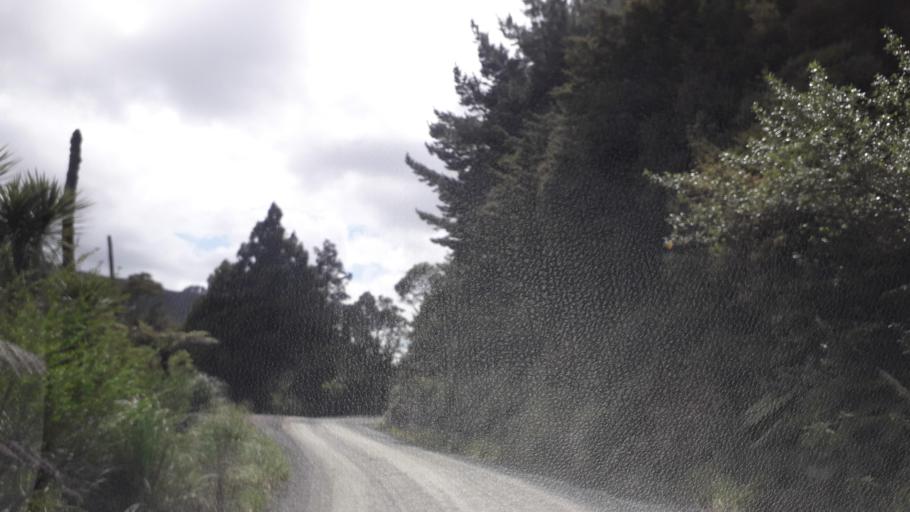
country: NZ
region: Northland
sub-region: Far North District
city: Kaitaia
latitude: -35.1874
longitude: 173.2952
